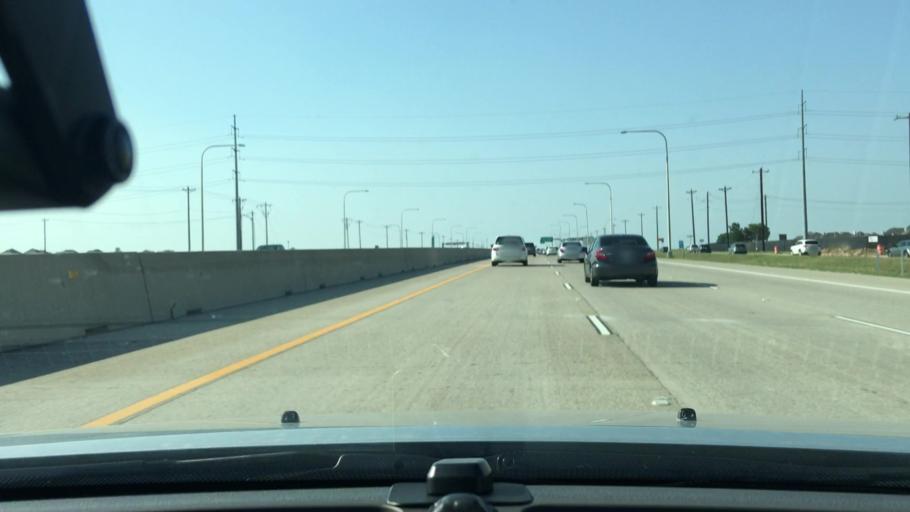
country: US
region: Texas
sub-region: Collin County
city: Frisco
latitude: 33.1809
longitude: -96.8393
